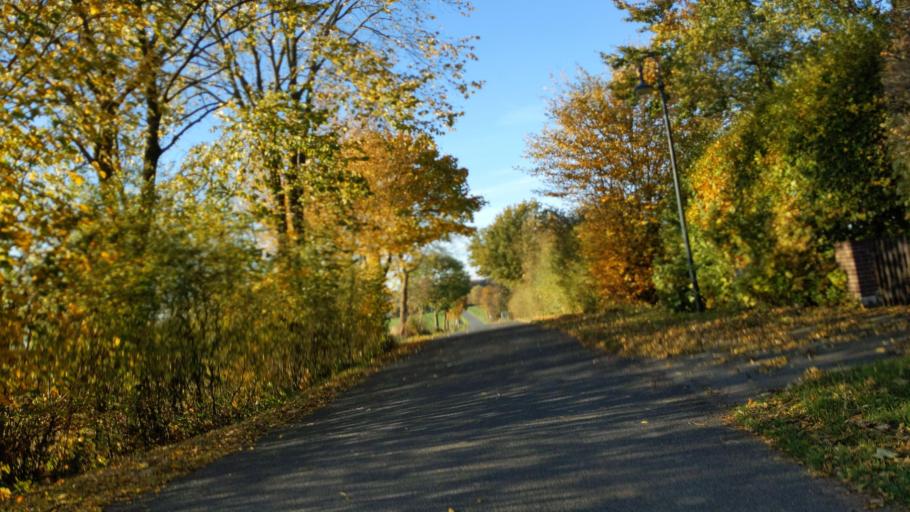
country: DE
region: Schleswig-Holstein
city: Gross Disnack
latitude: 53.7401
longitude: 10.7038
